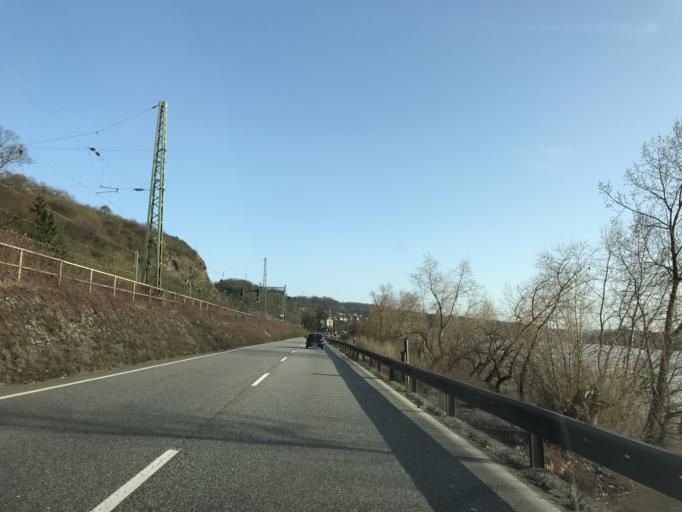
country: DE
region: Rheinland-Pfalz
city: Kasbach-Ohlenberg
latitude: 50.5763
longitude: 7.2655
